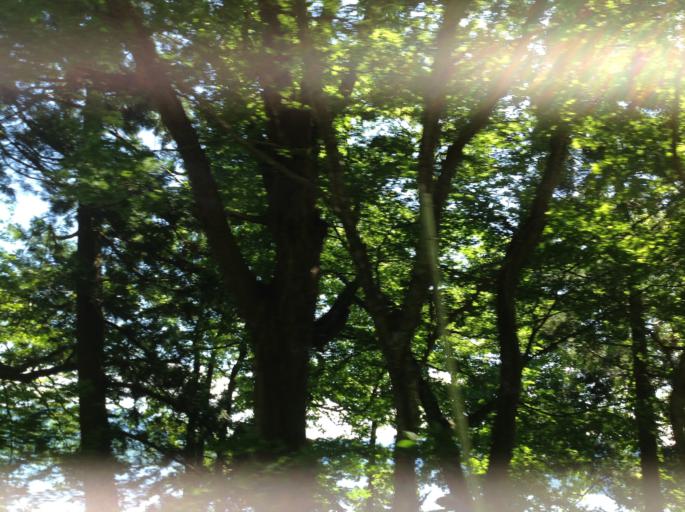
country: JP
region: Akita
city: Kakunodatemachi
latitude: 39.7025
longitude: 140.6445
